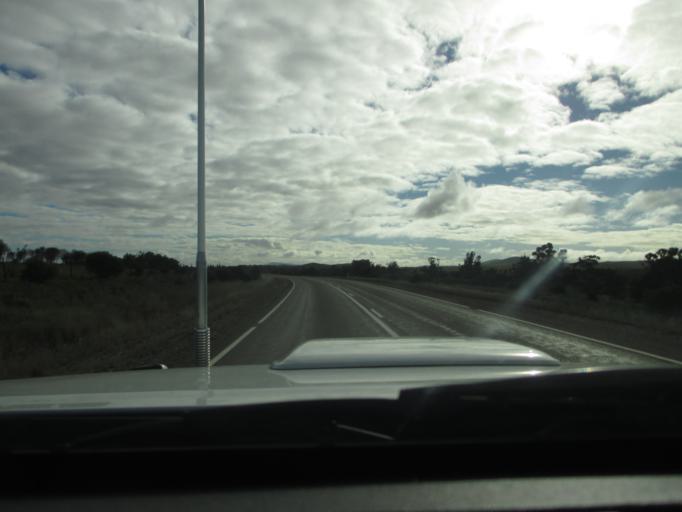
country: AU
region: South Australia
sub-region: Flinders Ranges
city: Quorn
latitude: -32.5009
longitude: 138.5480
